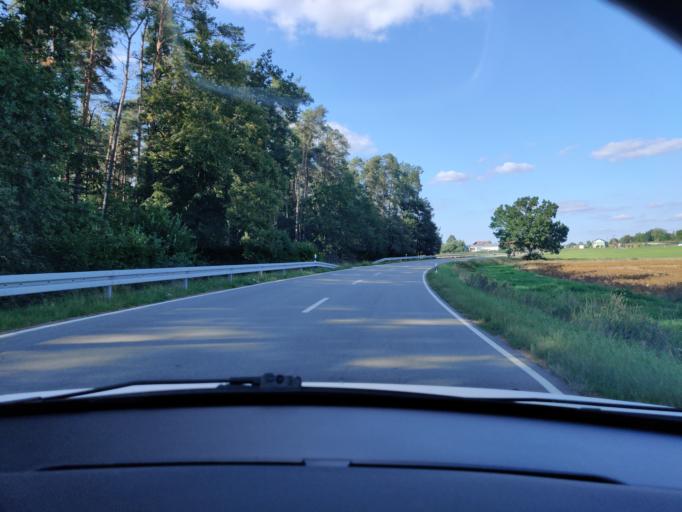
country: DE
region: Bavaria
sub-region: Upper Palatinate
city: Schwarzenfeld
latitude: 49.3566
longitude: 12.1470
